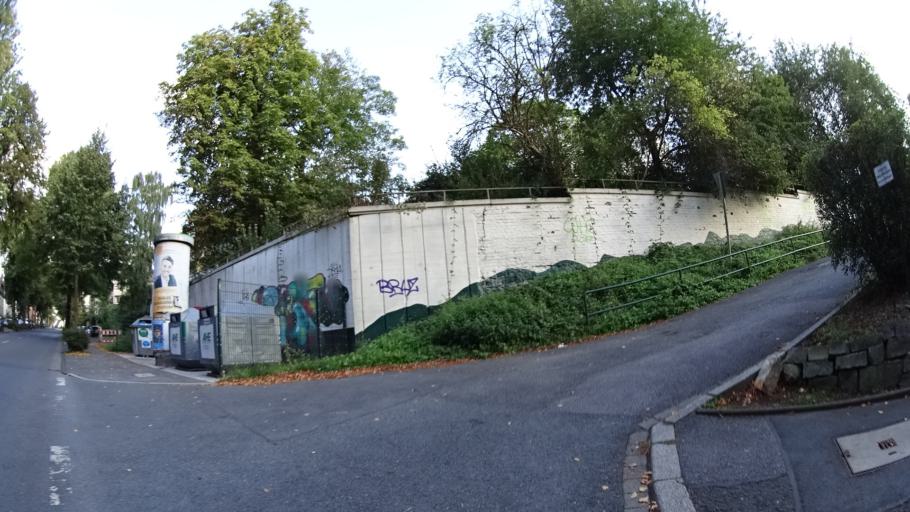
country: DE
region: North Rhine-Westphalia
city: Witten
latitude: 51.4360
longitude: 7.3533
